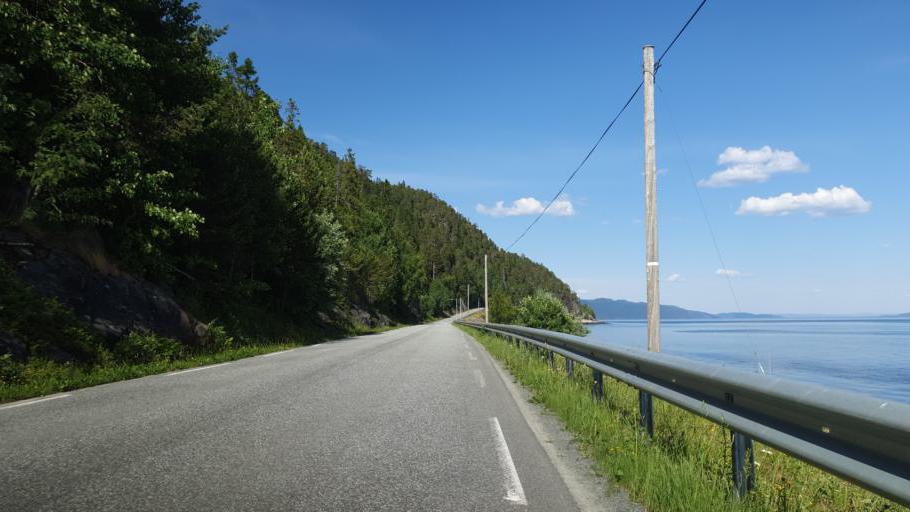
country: NO
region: Nord-Trondelag
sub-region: Leksvik
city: Leksvik
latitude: 63.6407
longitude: 10.5893
